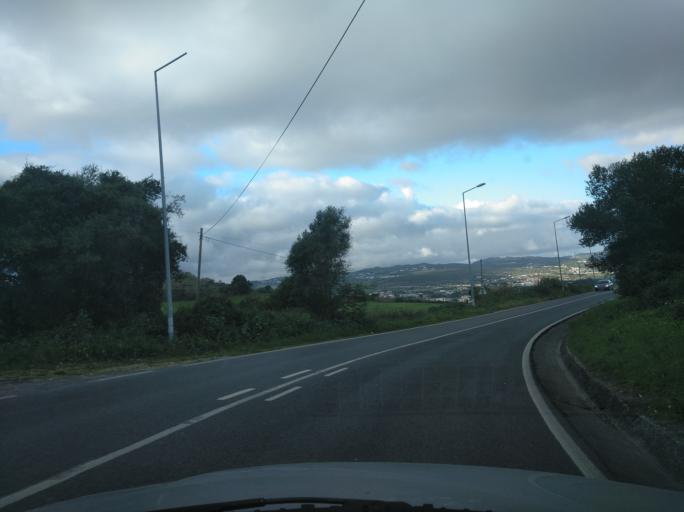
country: PT
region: Lisbon
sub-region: Loures
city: Loures
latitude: 38.8211
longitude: -9.1796
